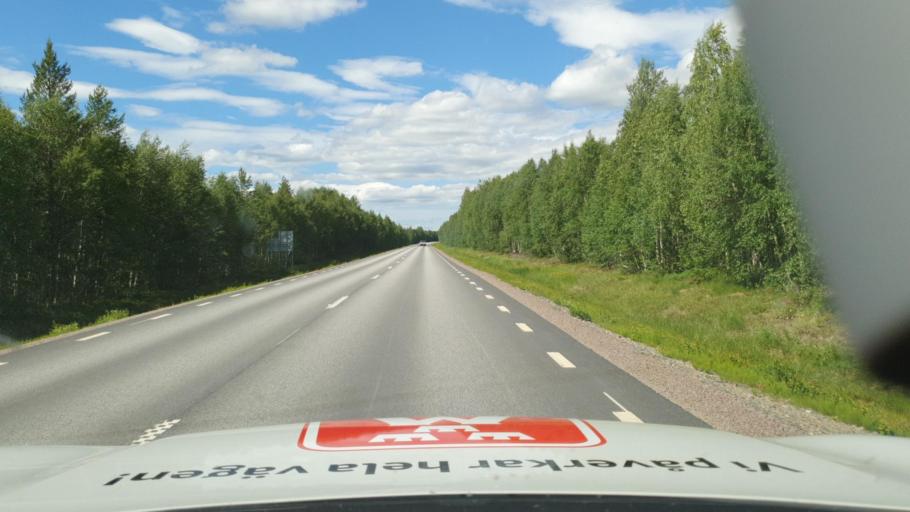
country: SE
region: Vaesterbotten
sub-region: Skelleftea Kommun
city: Langsele
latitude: 65.0678
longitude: 20.0347
